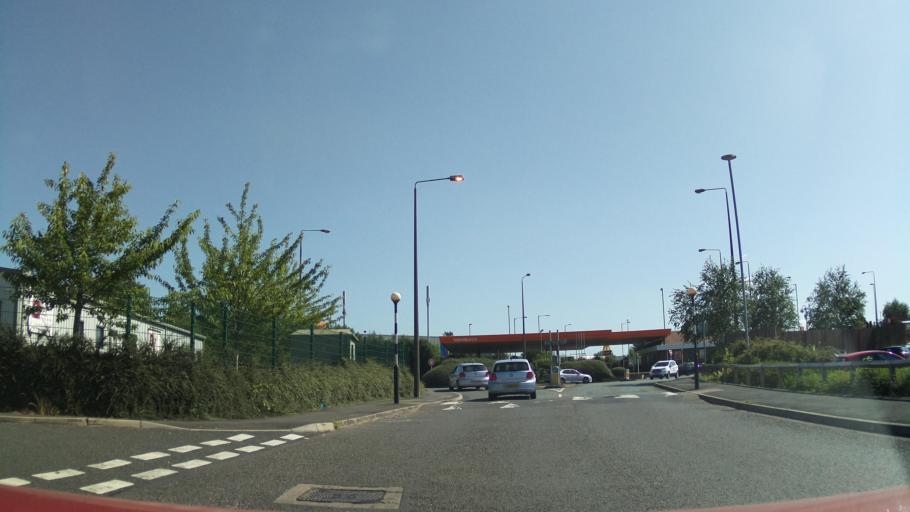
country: GB
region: England
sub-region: Derby
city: Derby
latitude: 52.8957
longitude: -1.4738
